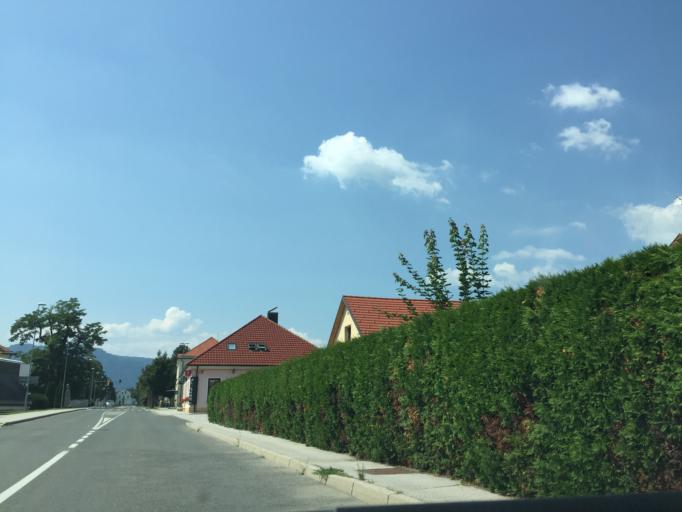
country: SI
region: Polzela
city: Polzela
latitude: 46.2787
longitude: 15.0797
